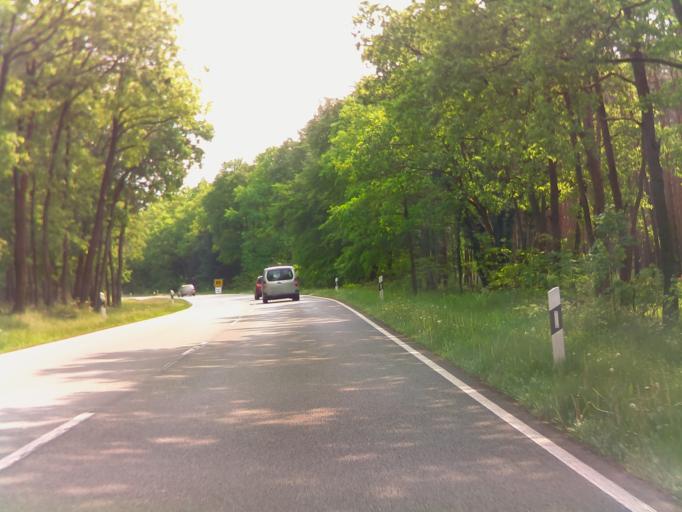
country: DE
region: Brandenburg
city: Rathenow
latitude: 52.6048
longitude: 12.3906
